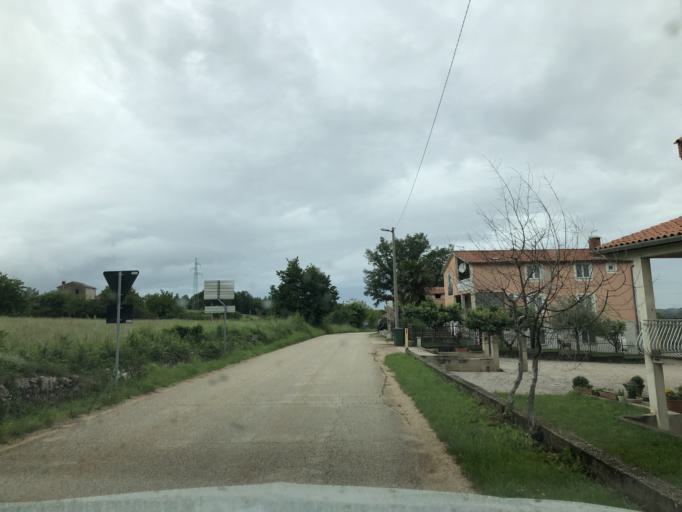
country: HR
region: Istarska
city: Buje
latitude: 45.4300
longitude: 13.6880
